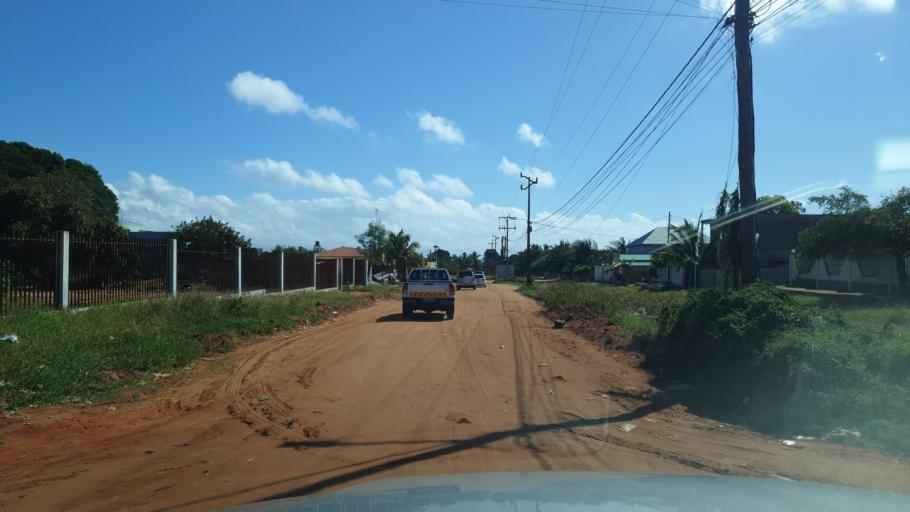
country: MZ
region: Cabo Delgado
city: Pemba
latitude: -12.9835
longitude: 40.5441
